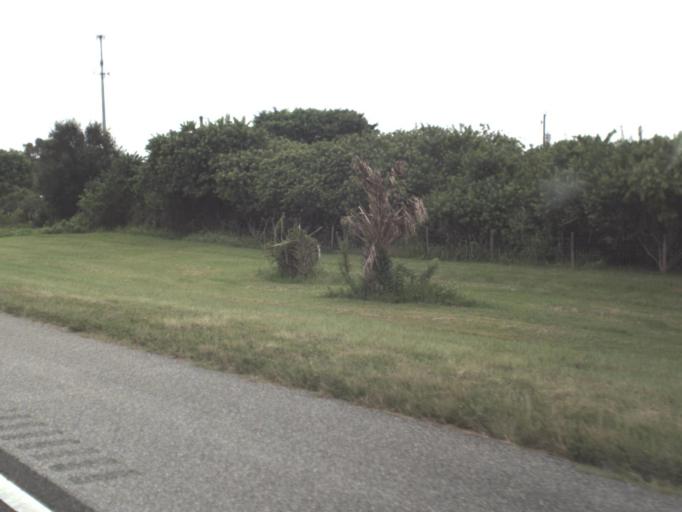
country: US
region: Florida
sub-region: Manatee County
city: Memphis
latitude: 27.5842
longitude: -82.5574
